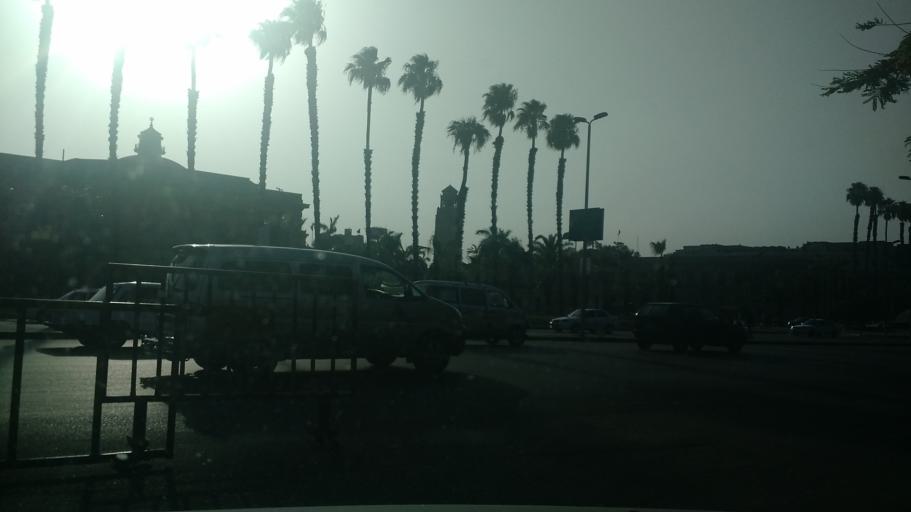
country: EG
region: Al Jizah
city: Al Jizah
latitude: 30.0267
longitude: 31.2111
